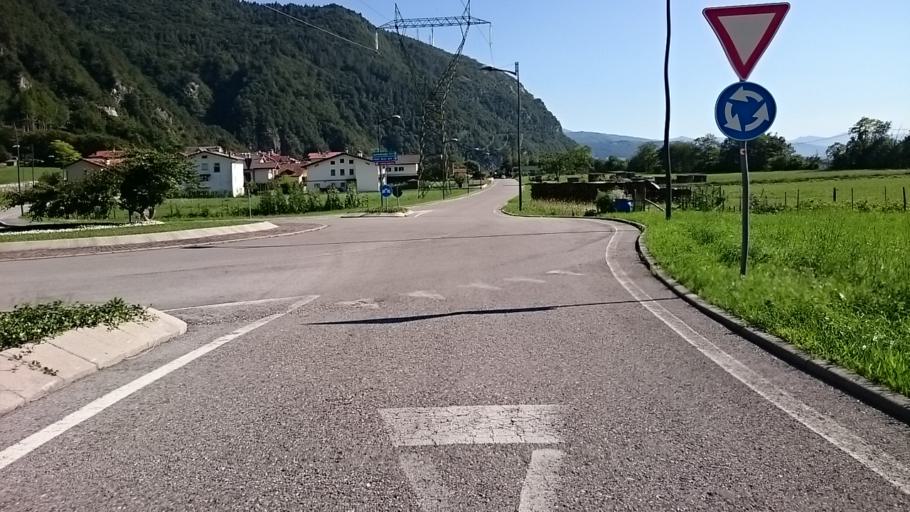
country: IT
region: Veneto
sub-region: Provincia di Belluno
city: Soverzene
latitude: 46.2082
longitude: 12.3021
